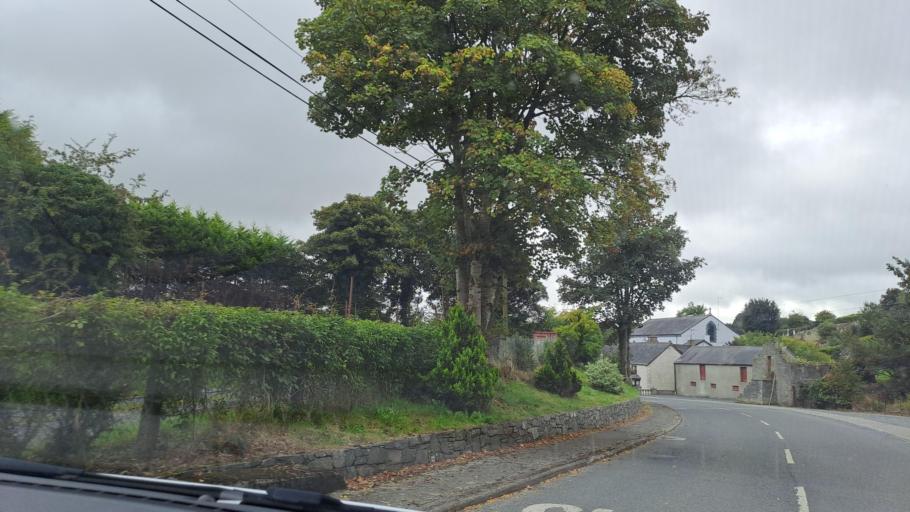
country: IE
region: Ulster
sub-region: County Monaghan
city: Carrickmacross
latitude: 54.0302
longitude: -6.7542
